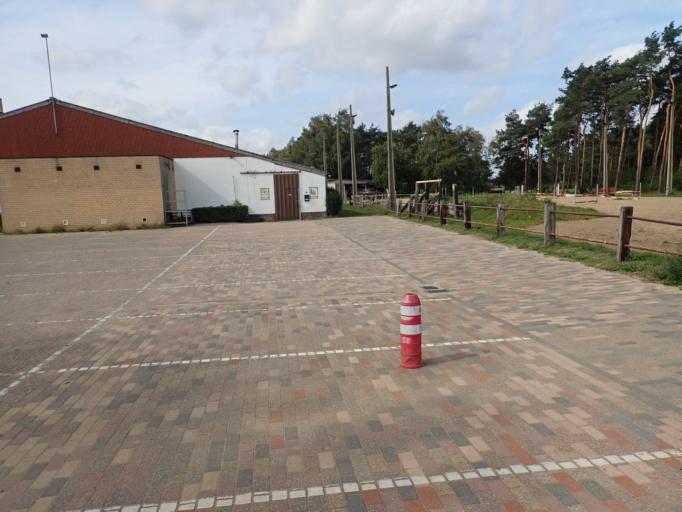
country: BE
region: Flanders
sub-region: Provincie Antwerpen
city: Lille
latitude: 51.2410
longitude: 4.8138
